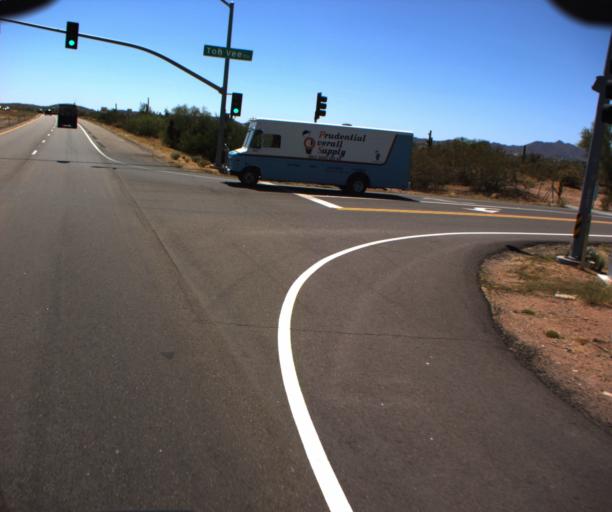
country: US
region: Arizona
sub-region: Maricopa County
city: Fountain Hills
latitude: 33.5782
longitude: -111.6856
